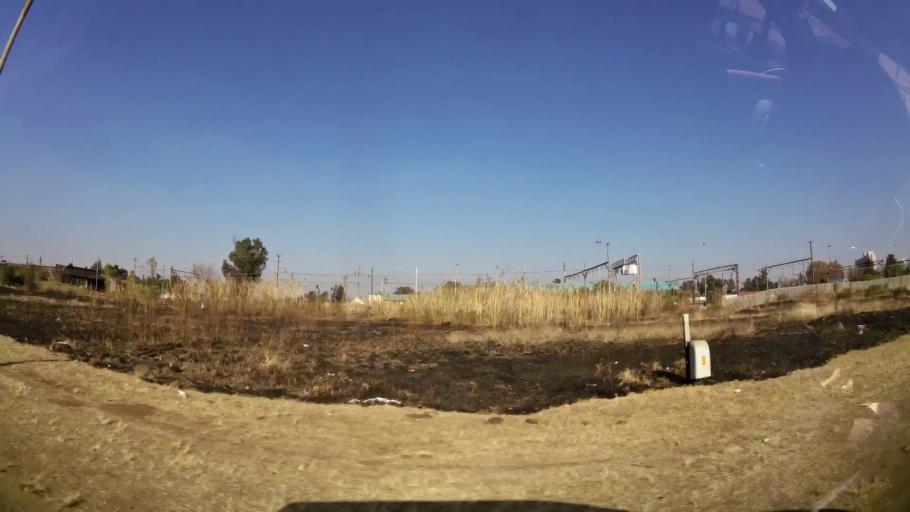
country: ZA
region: Gauteng
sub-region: West Rand District Municipality
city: Randfontein
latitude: -26.1564
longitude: 27.7160
